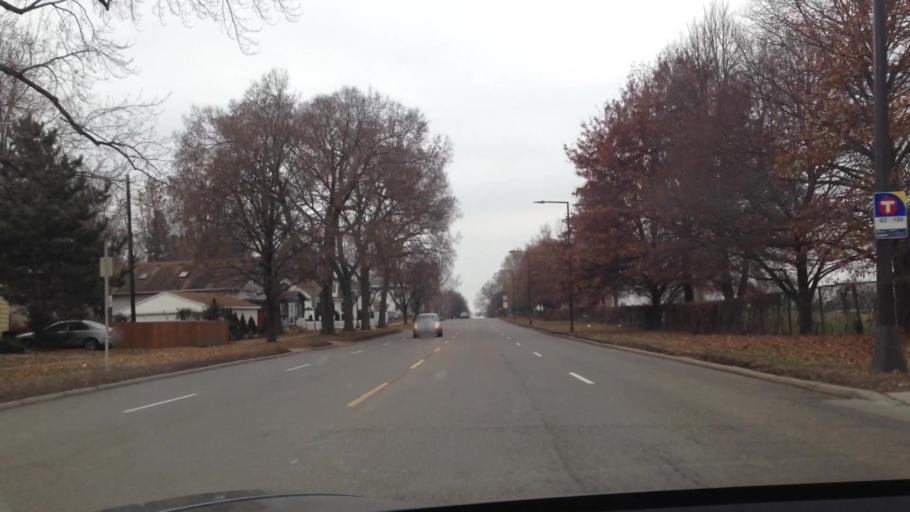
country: US
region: Minnesota
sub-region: Ramsey County
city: Falcon Heights
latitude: 44.9542
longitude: -93.1925
